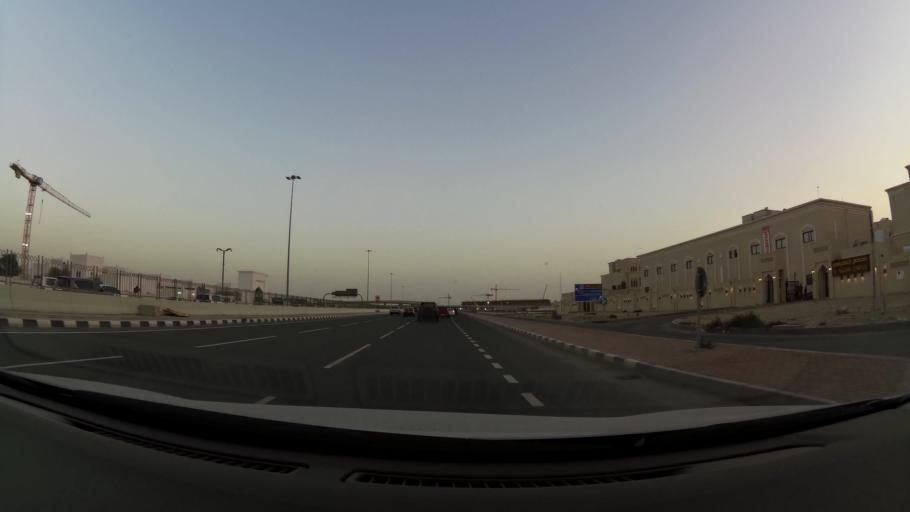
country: QA
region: Baladiyat ar Rayyan
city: Ar Rayyan
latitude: 25.3017
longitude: 51.4736
